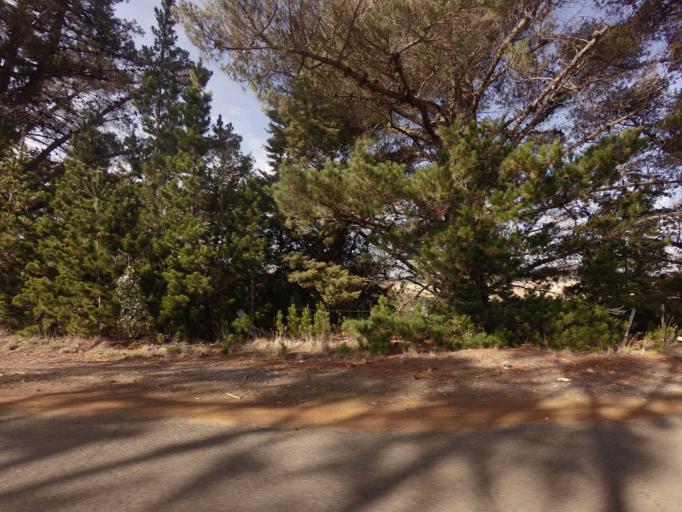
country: AU
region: Tasmania
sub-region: Sorell
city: Sorell
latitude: -42.4387
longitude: 147.4724
